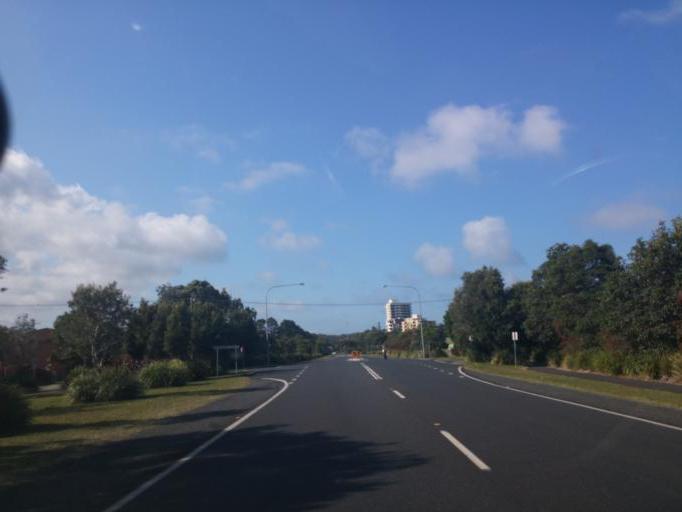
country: AU
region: New South Wales
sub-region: Coffs Harbour
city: Coffs Harbour
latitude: -30.2881
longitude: 153.1358
